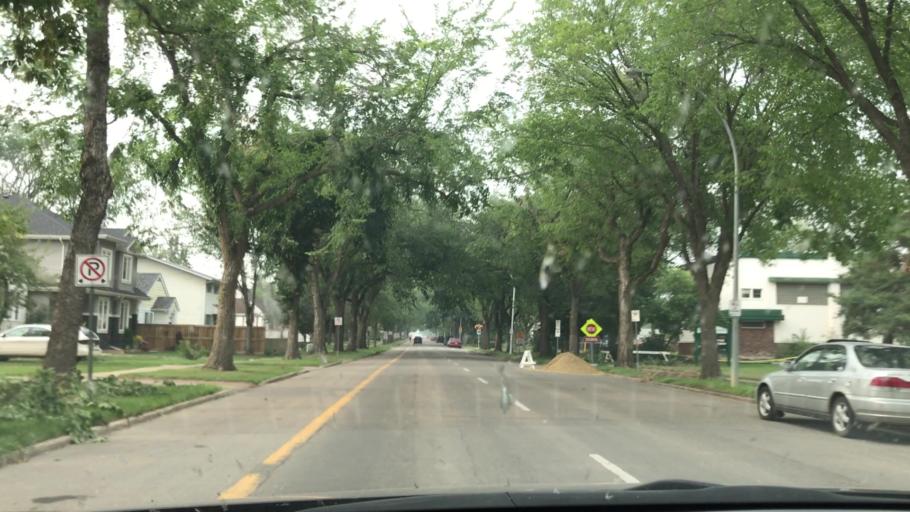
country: CA
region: Alberta
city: Edmonton
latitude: 53.5655
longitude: -113.5412
